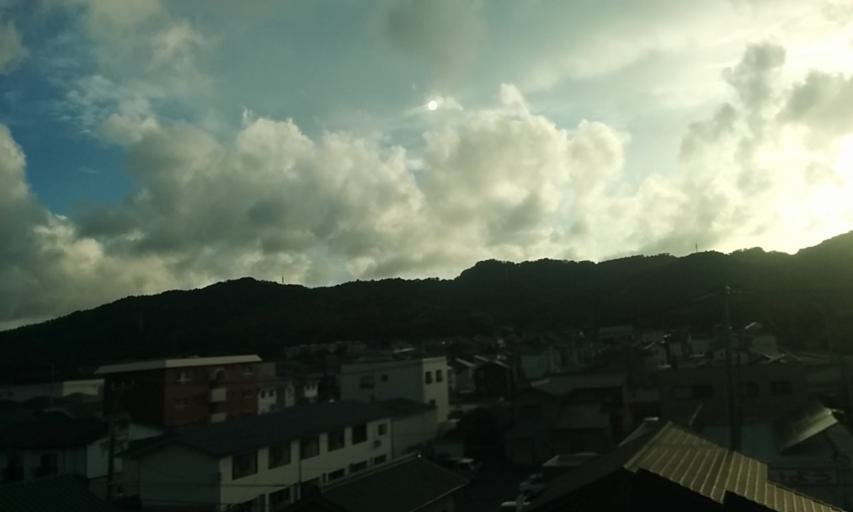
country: JP
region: Aichi
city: Gamagori
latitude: 34.8579
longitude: 137.1643
